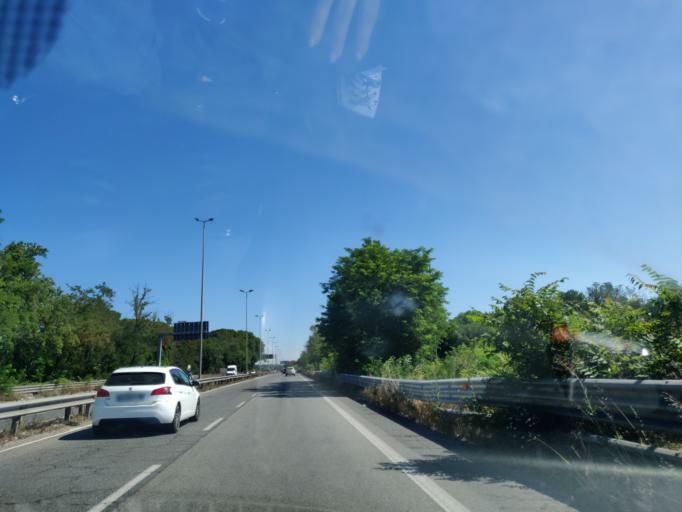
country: IT
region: Latium
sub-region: Citta metropolitana di Roma Capitale
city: Selcetta
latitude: 41.8097
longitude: 12.4581
